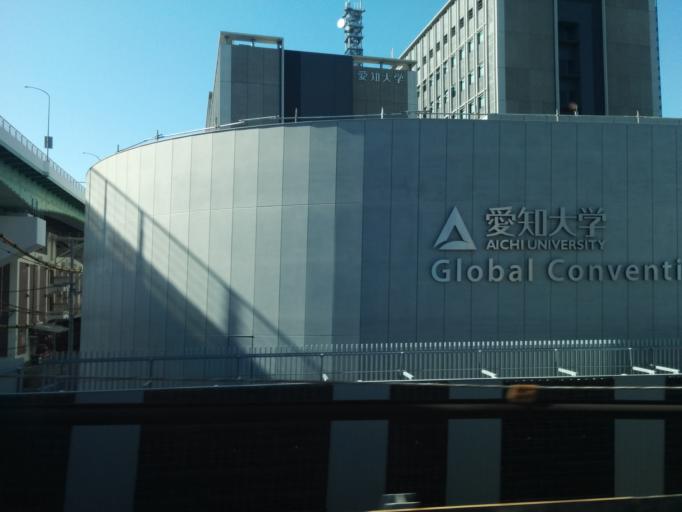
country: JP
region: Aichi
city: Nagoya-shi
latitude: 35.1612
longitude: 136.8858
